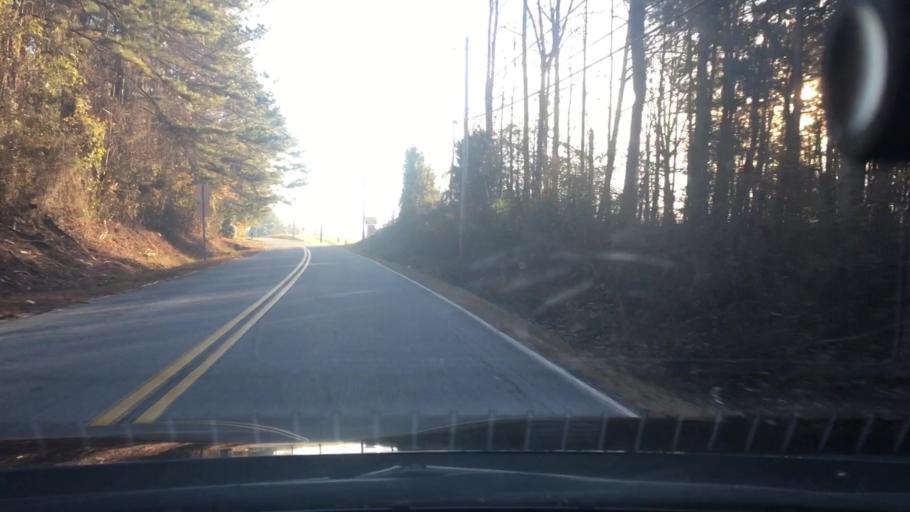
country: US
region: Georgia
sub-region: Spalding County
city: Experiment
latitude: 33.2611
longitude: -84.2976
